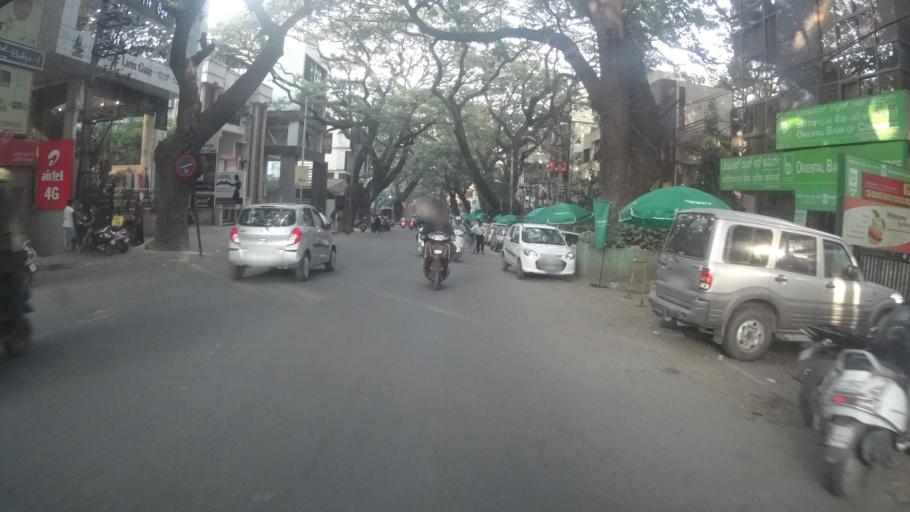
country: IN
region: Karnataka
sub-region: Bangalore Urban
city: Bangalore
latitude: 12.9964
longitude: 77.6139
